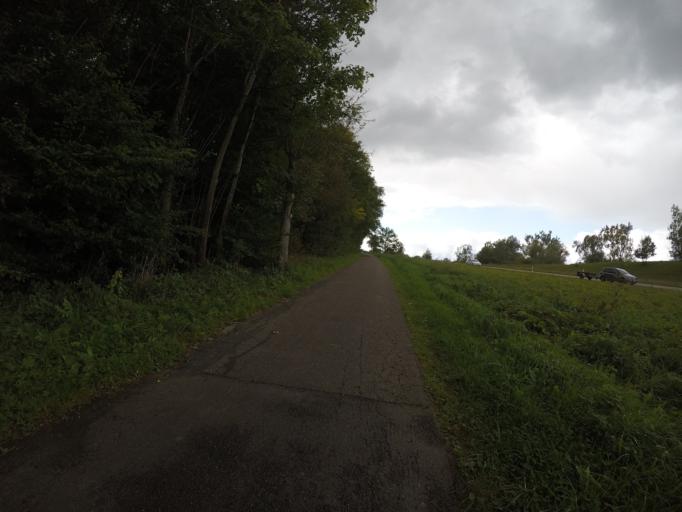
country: DE
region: Baden-Wuerttemberg
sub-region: Tuebingen Region
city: Reutlingen
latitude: 48.4728
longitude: 9.1710
